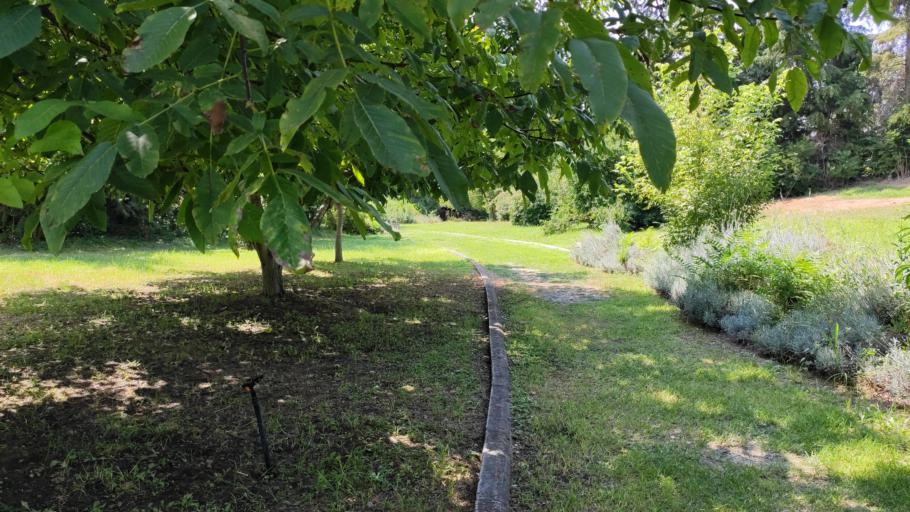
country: GR
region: Central Macedonia
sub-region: Nomos Imathias
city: Vergina
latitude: 40.4871
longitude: 22.3200
